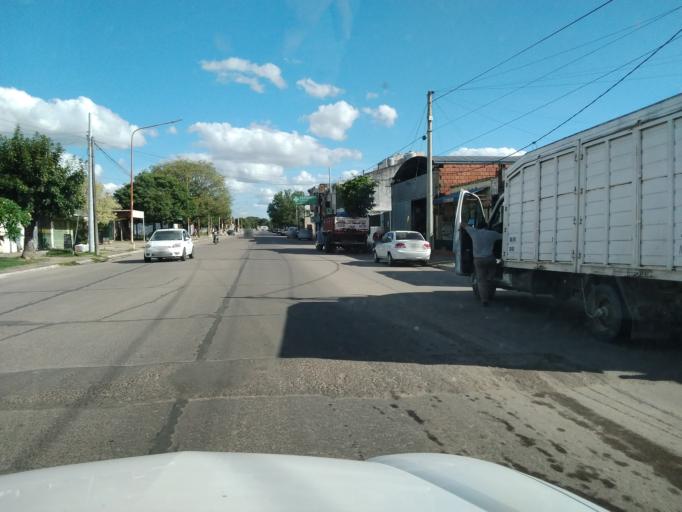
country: AR
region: Corrientes
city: Corrientes
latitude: -27.4936
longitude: -58.8336
